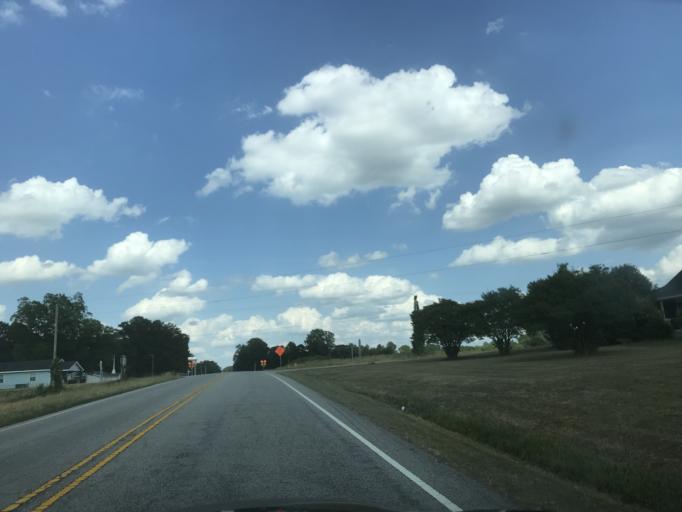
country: US
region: North Carolina
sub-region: Wake County
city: Rolesville
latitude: 35.9675
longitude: -78.4056
